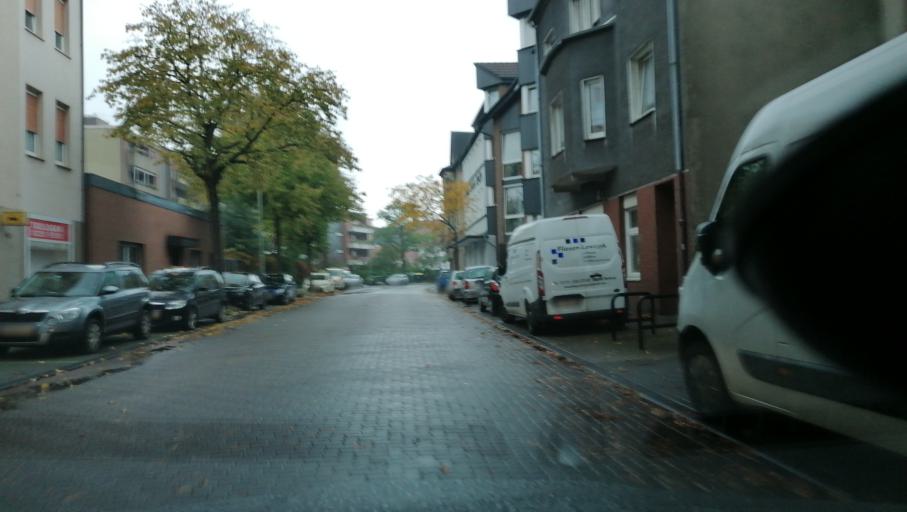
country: DE
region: North Rhine-Westphalia
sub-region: Regierungsbezirk Munster
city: Gelsenkirchen
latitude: 51.5428
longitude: 7.1458
